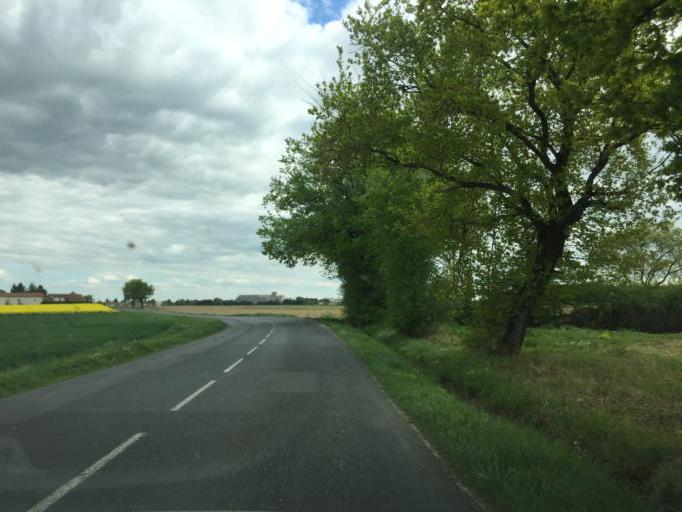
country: FR
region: Rhone-Alpes
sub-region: Departement de l'Ain
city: Saint-Andre-de-Corcy
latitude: 45.9389
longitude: 4.9431
